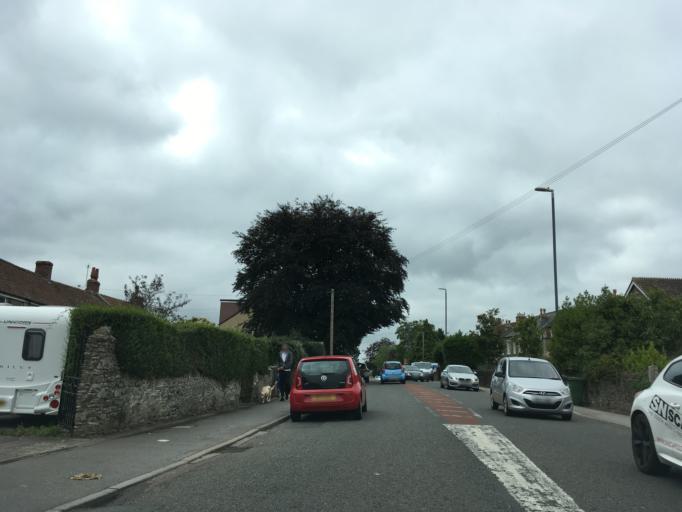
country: GB
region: England
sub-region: South Gloucestershire
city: Bitton
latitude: 51.4415
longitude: -2.4682
